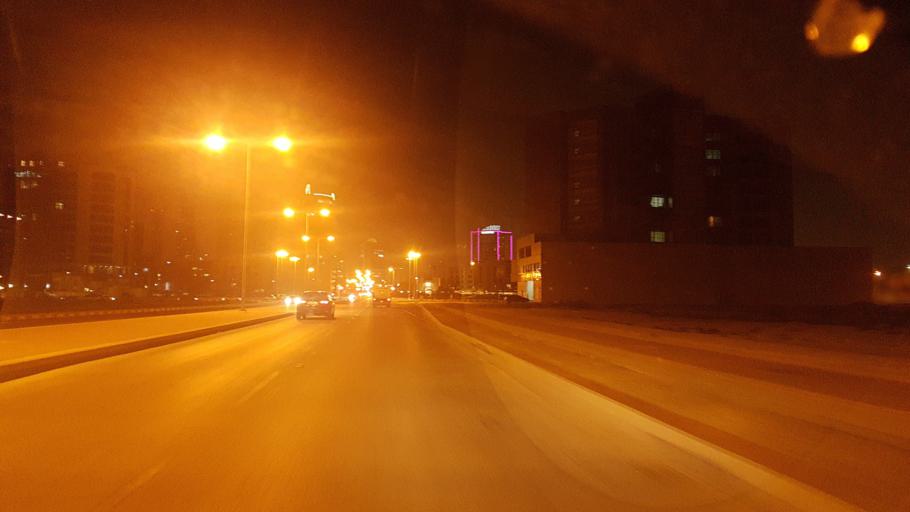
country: BH
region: Manama
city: Jidd Hafs
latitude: 26.2369
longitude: 50.5271
